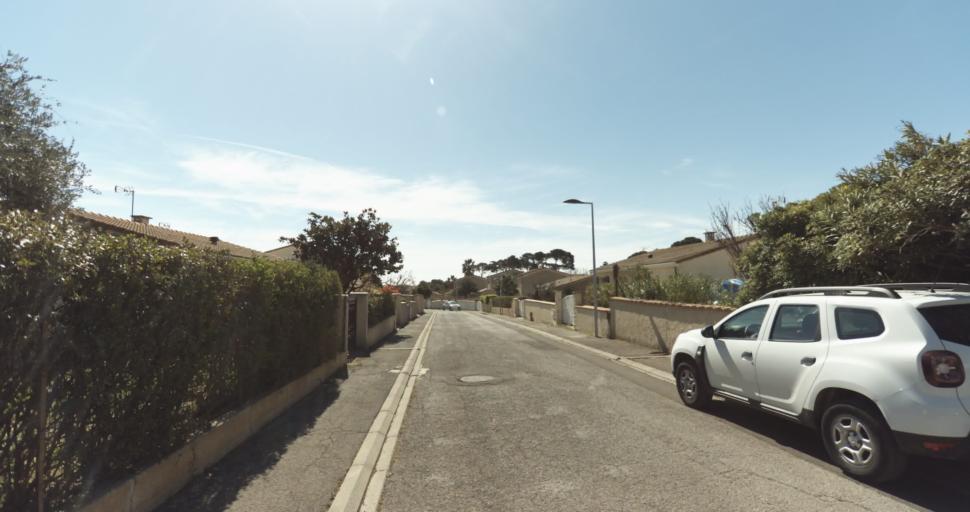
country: FR
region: Languedoc-Roussillon
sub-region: Departement de l'Herault
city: Marseillan
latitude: 43.3585
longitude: 3.5314
